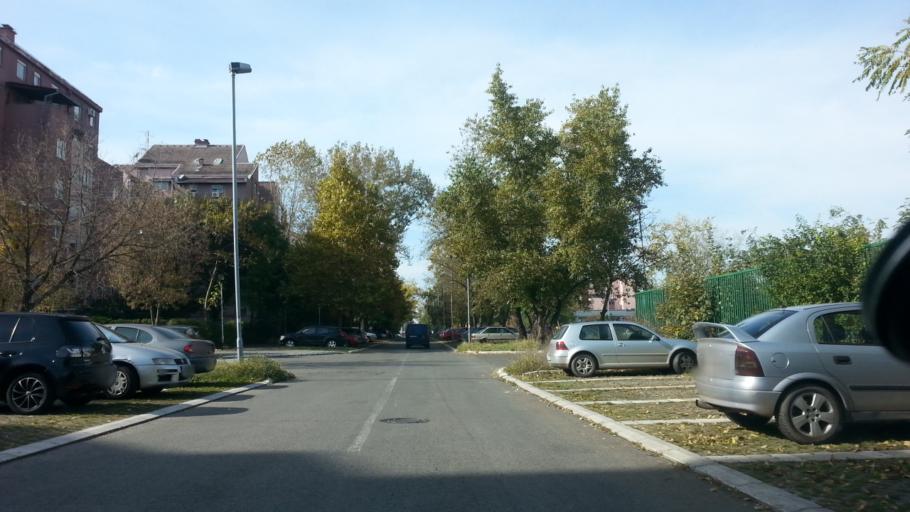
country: RS
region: Central Serbia
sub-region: Belgrade
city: Zemun
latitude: 44.8151
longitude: 20.3771
